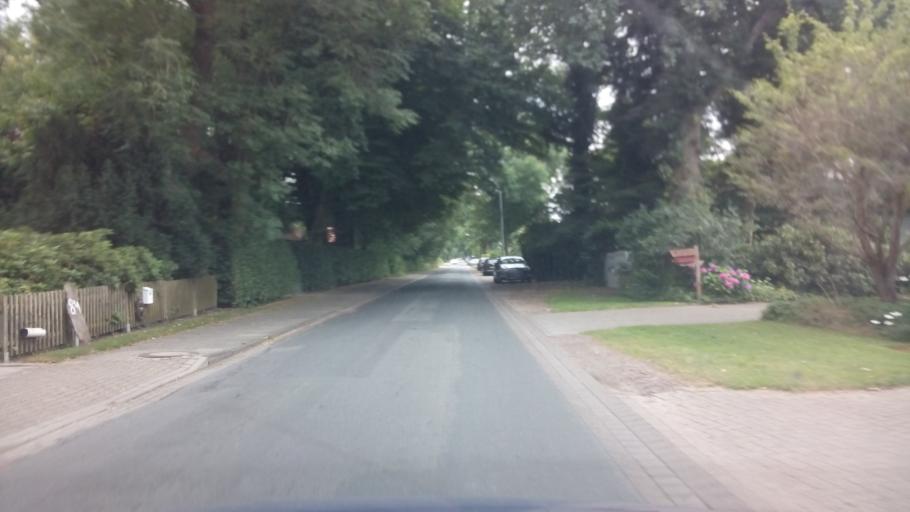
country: DE
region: Lower Saxony
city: Ritterhude
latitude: 53.2119
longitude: 8.7510
